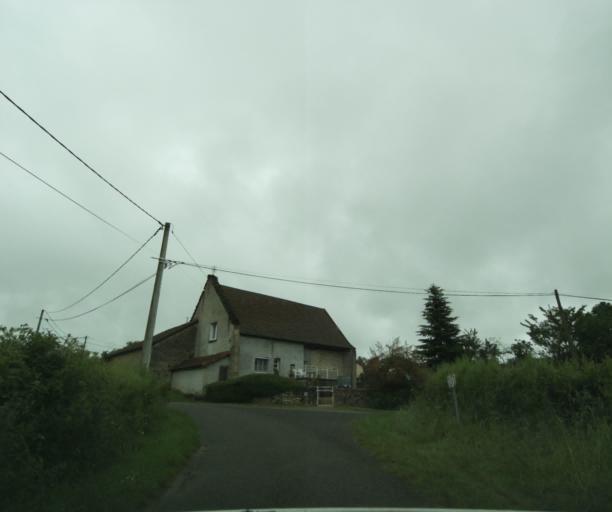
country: FR
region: Bourgogne
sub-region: Departement de Saone-et-Loire
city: Charolles
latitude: 46.4391
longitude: 4.3189
